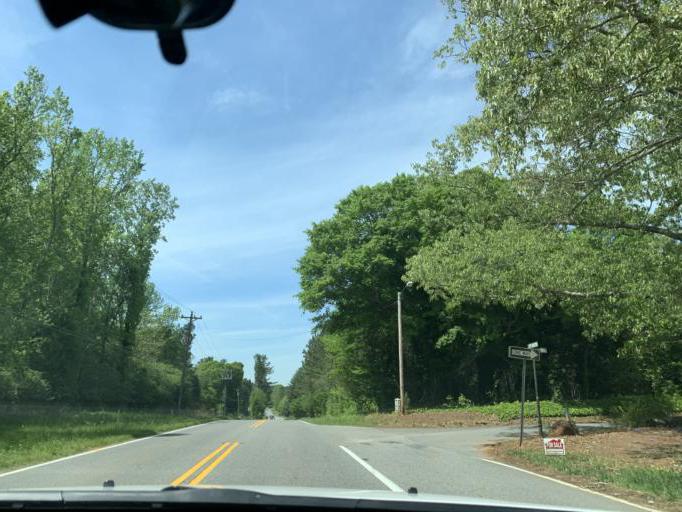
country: US
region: Georgia
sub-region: Forsyth County
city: Cumming
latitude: 34.2601
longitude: -84.1713
